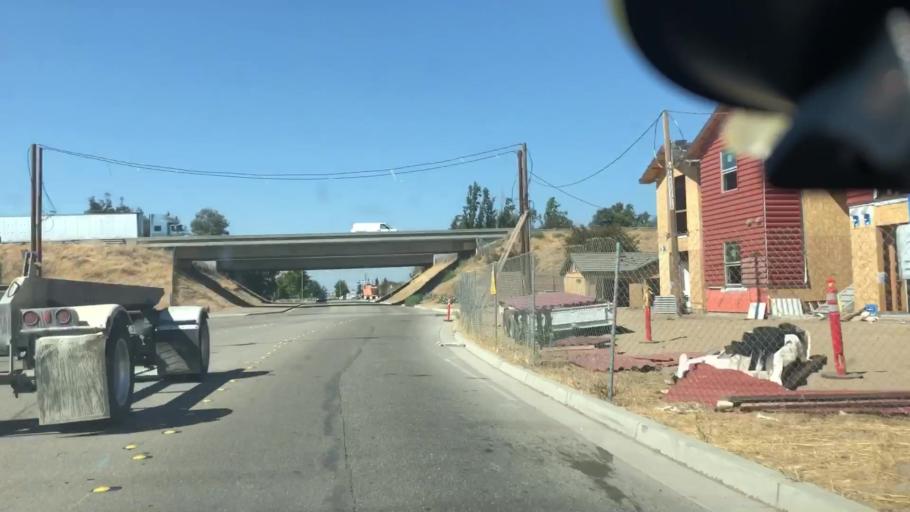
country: US
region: California
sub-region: San Joaquin County
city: Manteca
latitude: 37.7823
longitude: -121.2006
